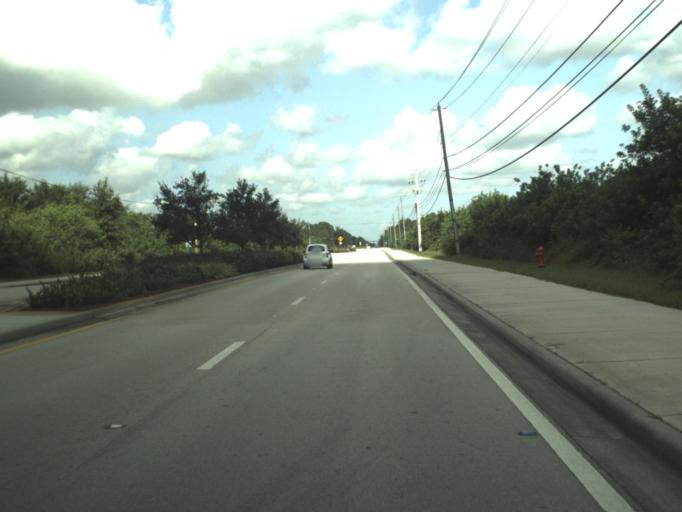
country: US
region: Florida
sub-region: Martin County
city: North River Shores
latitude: 27.2096
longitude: -80.3452
